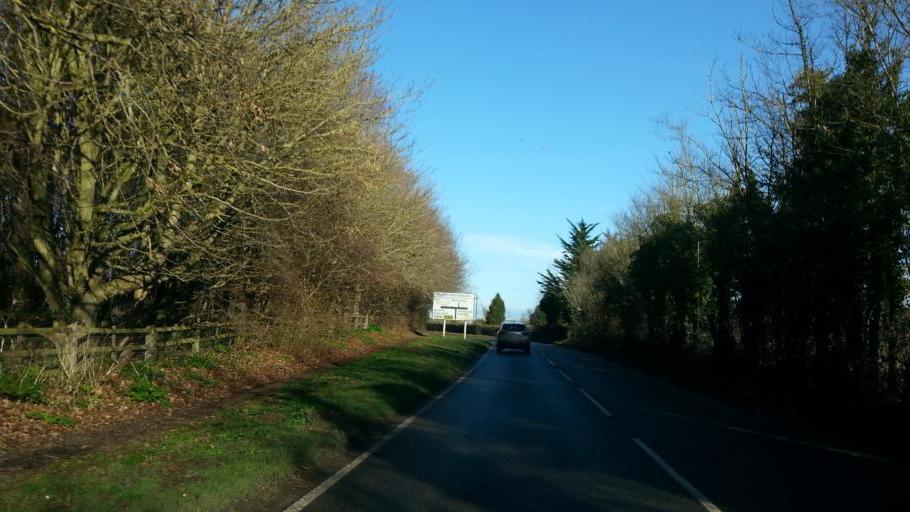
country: GB
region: England
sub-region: Suffolk
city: Saxmundham
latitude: 52.1773
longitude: 1.5020
